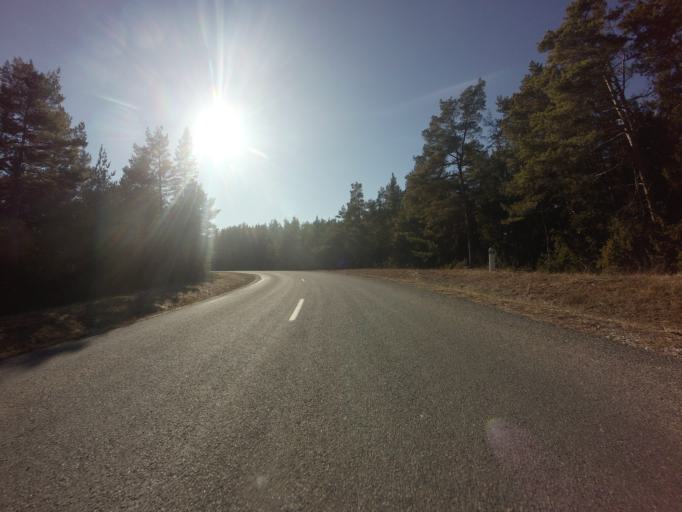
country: EE
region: Saare
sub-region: Kuressaare linn
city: Kuressaare
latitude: 58.5131
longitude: 22.3164
